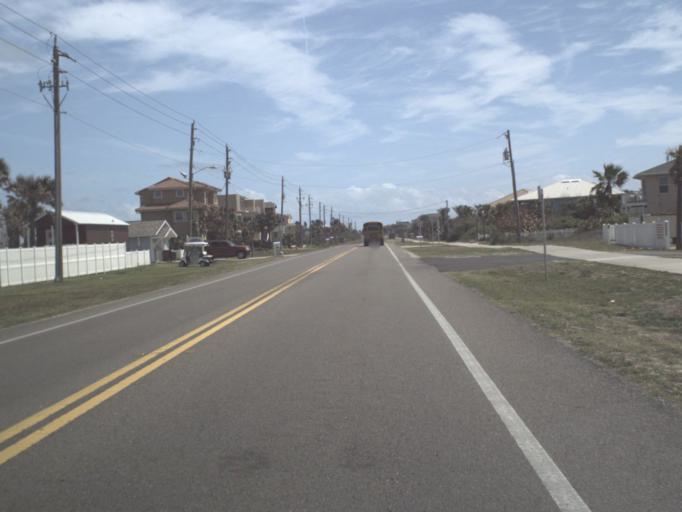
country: US
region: Florida
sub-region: Flagler County
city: Flagler Beach
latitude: 29.5209
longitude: -81.1475
